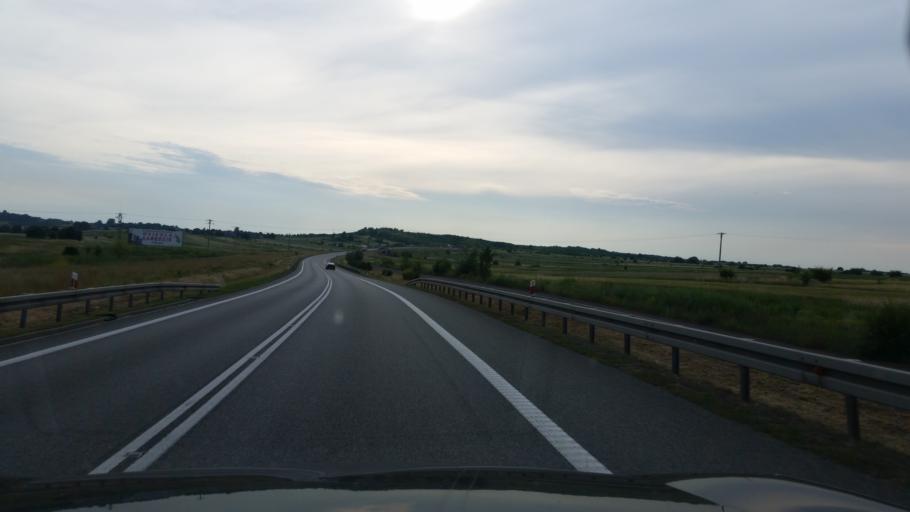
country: PL
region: Silesian Voivodeship
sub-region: Powiat bedzinski
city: Mierzecice
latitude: 50.4249
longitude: 19.1726
